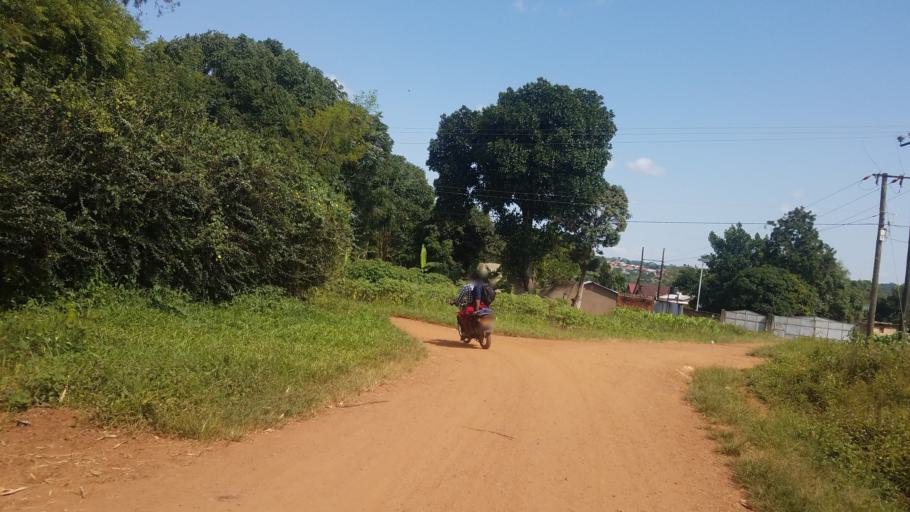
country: UG
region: Central Region
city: Masaka
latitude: -0.3334
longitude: 31.7200
